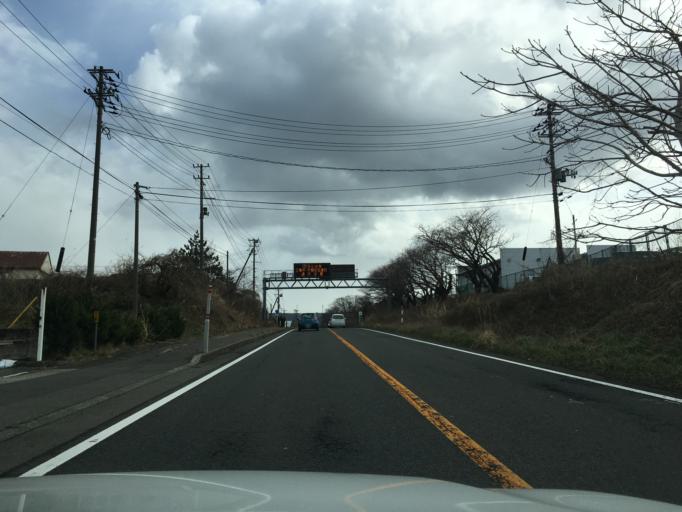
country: JP
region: Yamagata
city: Yuza
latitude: 39.2811
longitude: 139.9378
